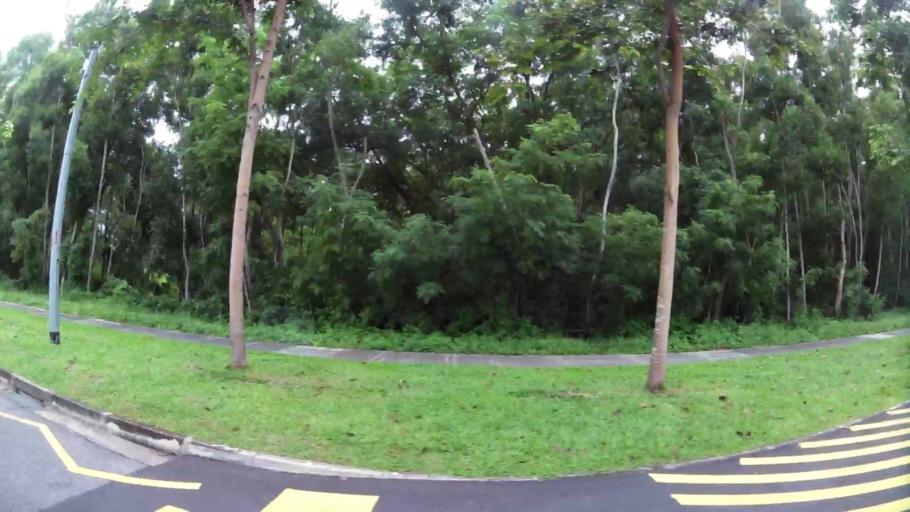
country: SG
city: Singapore
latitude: 1.3562
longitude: 103.9753
